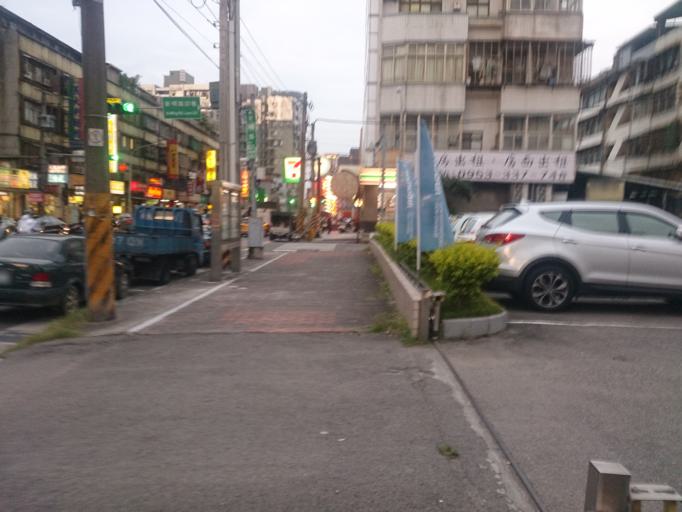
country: TW
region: Taipei
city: Taipei
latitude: 25.0567
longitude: 121.5843
